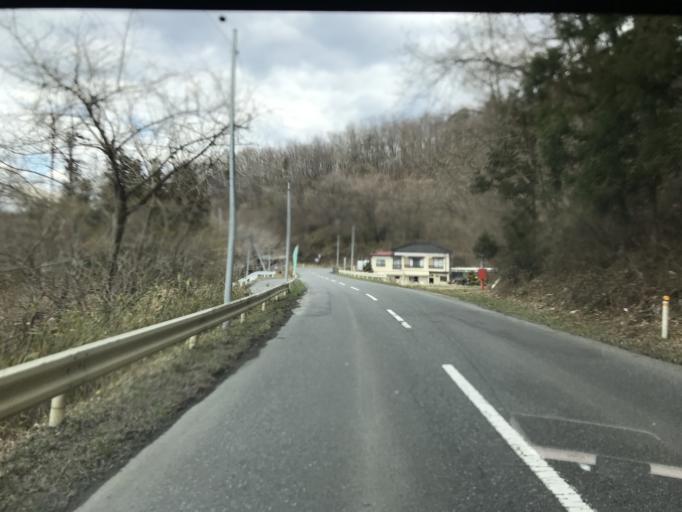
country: JP
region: Iwate
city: Ichinoseki
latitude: 38.8423
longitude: 141.3417
